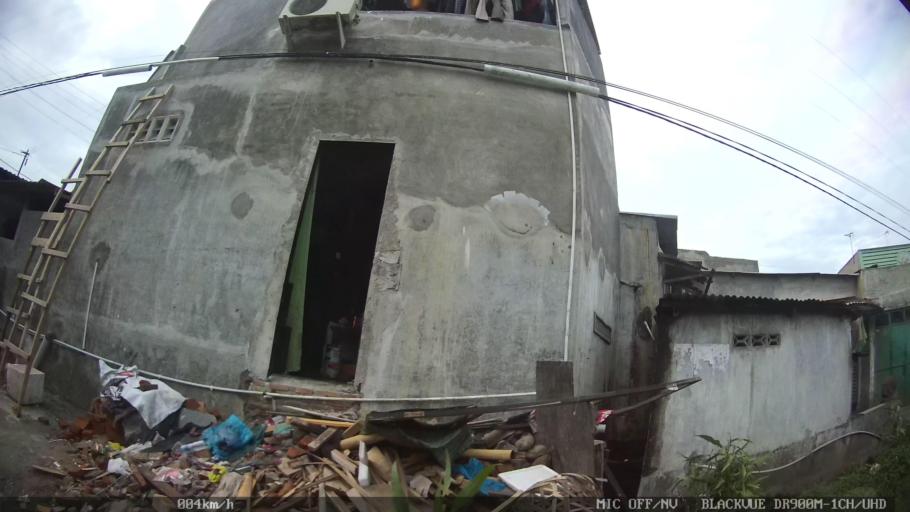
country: ID
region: North Sumatra
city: Sunggal
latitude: 3.5729
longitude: 98.5848
